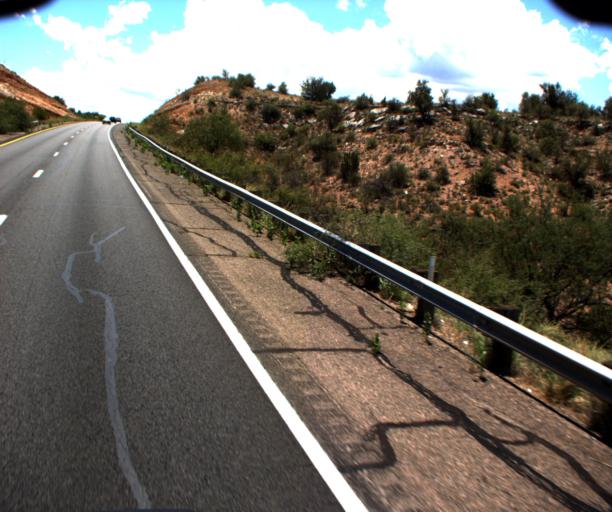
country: US
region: Arizona
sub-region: Yavapai County
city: Verde Village
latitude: 34.6760
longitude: -111.9722
